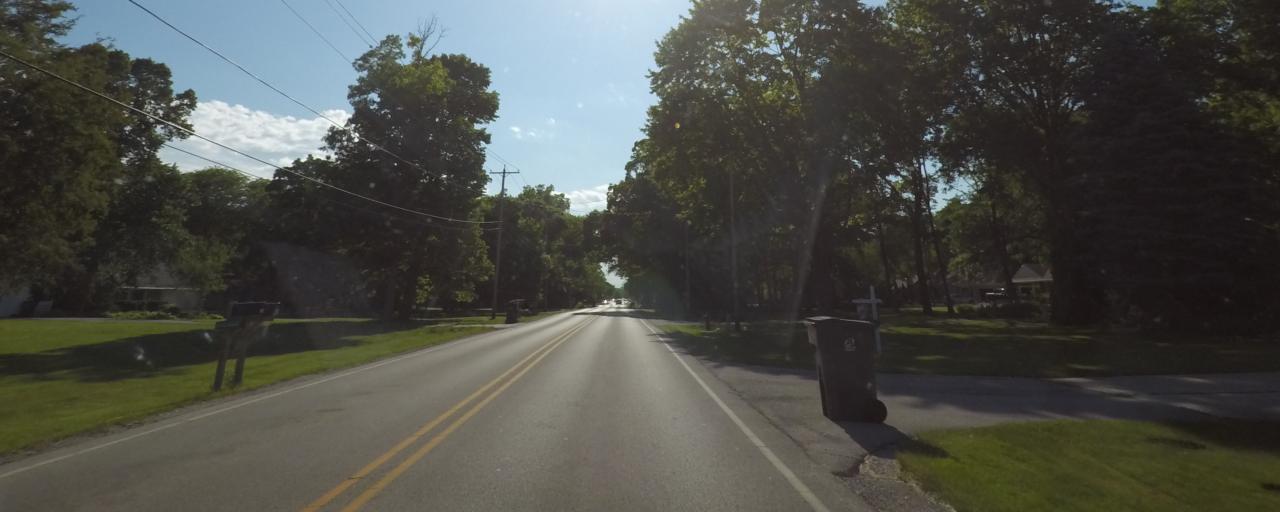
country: US
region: Wisconsin
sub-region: Milwaukee County
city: Hales Corners
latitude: 42.9448
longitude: -88.0403
